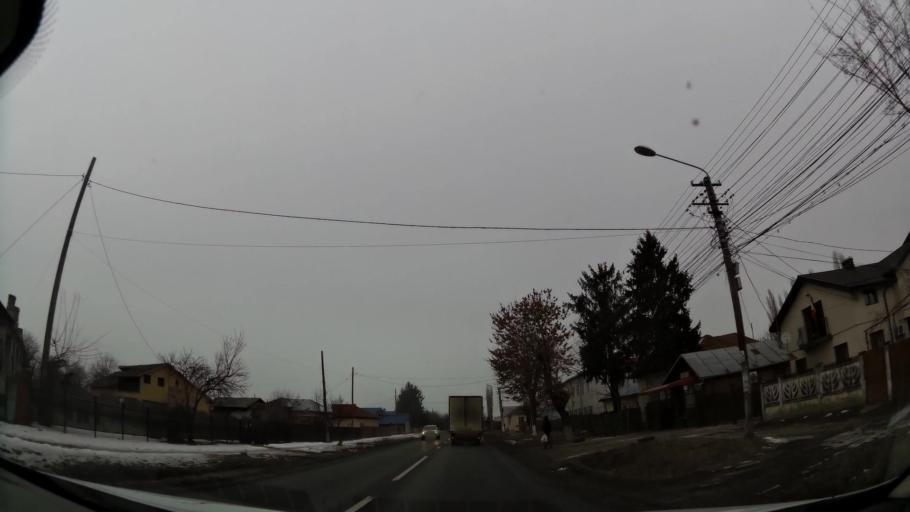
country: RO
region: Dambovita
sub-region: Comuna Racari
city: Racari
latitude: 44.6298
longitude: 25.7317
